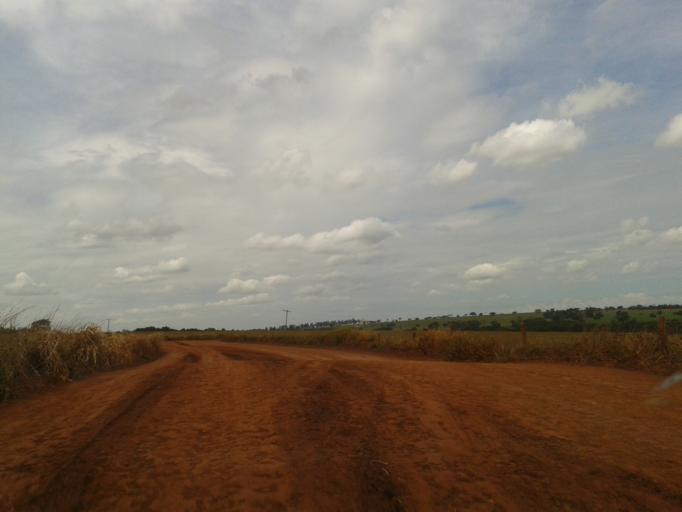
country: BR
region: Minas Gerais
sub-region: Centralina
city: Centralina
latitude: -18.7662
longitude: -49.2479
